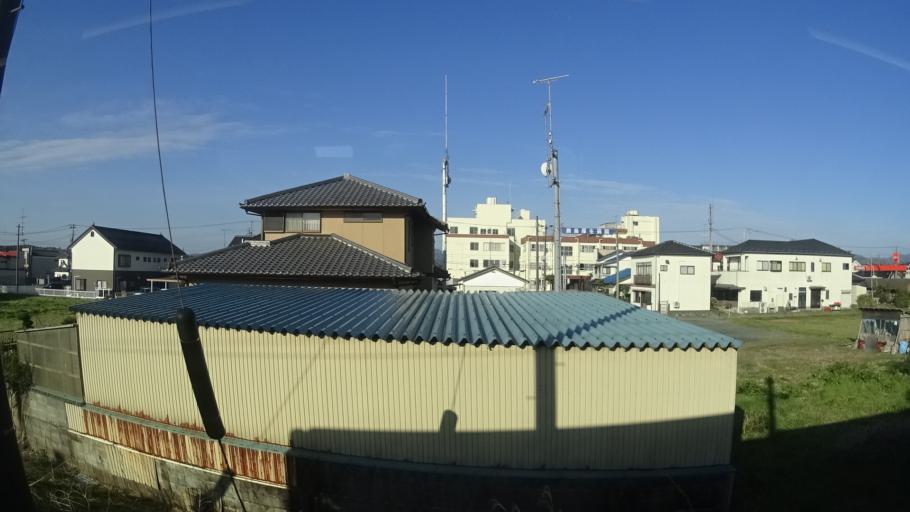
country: JP
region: Fukushima
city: Namie
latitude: 37.7091
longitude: 140.9647
